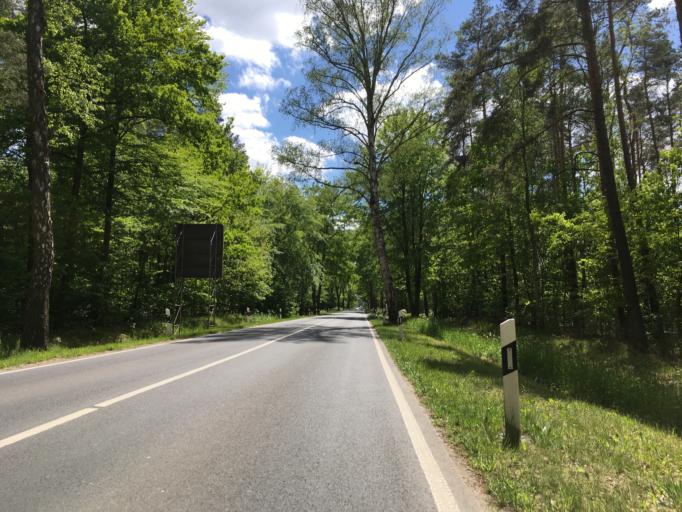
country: DE
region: Brandenburg
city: Rudnitz
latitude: 52.7697
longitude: 13.5648
